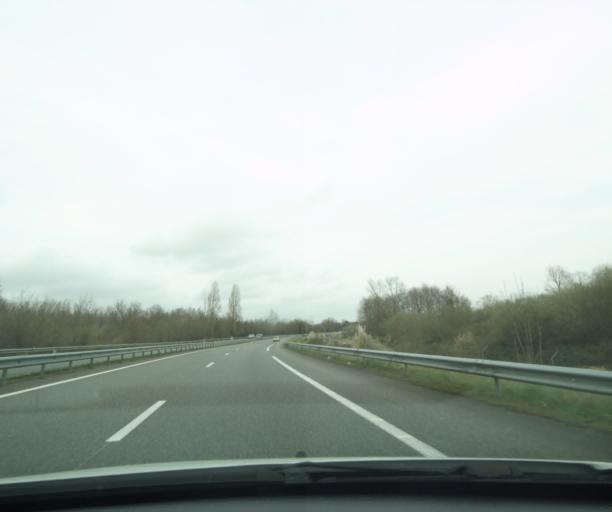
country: FR
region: Aquitaine
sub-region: Departement des Pyrenees-Atlantiques
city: Bardos
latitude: 43.5271
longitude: -1.2041
